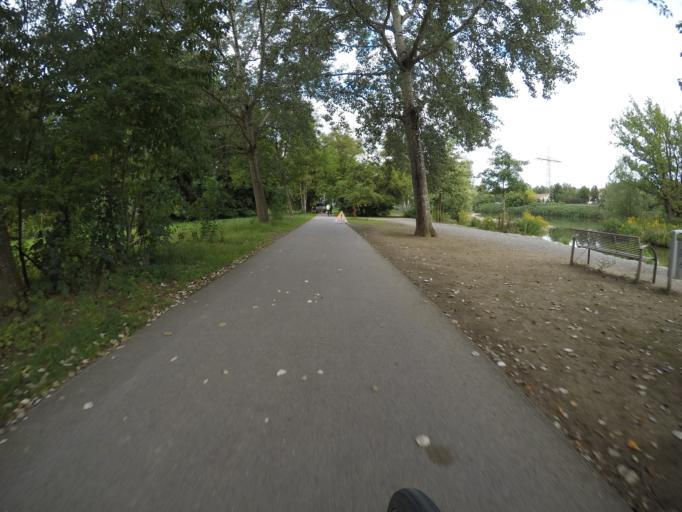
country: DE
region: Baden-Wuerttemberg
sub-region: Regierungsbezirk Stuttgart
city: Freiberg am Neckar
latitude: 48.9104
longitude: 9.2169
